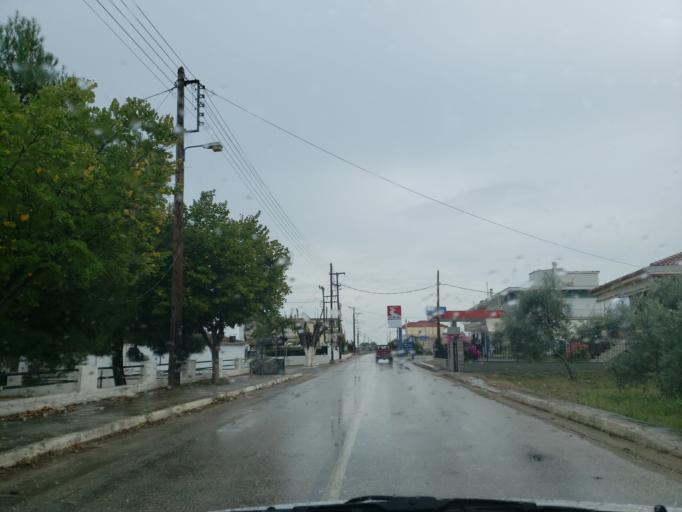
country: GR
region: Central Greece
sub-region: Nomos Fthiotidos
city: Anthili
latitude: 38.8045
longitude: 22.4460
